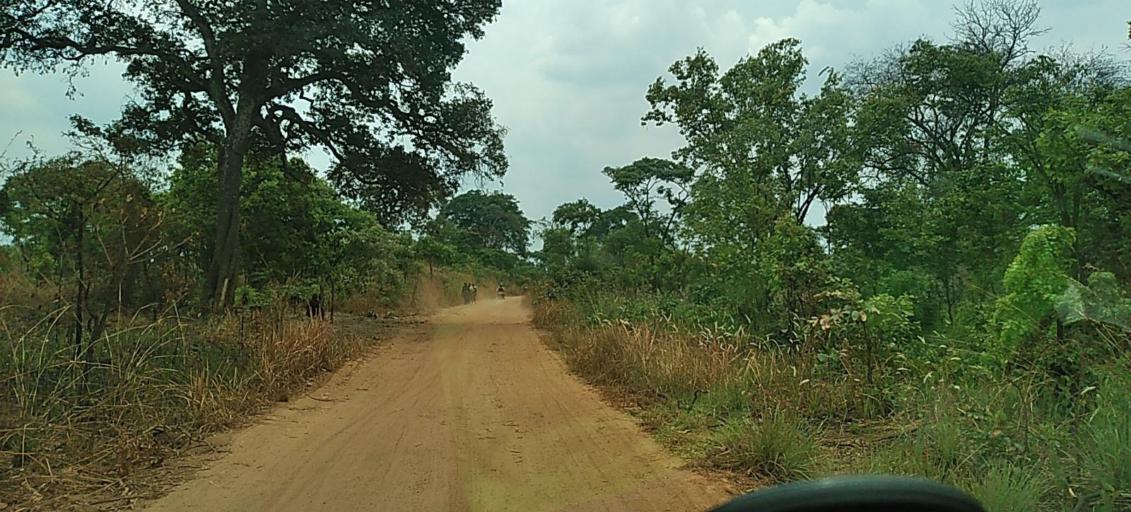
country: ZM
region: North-Western
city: Kansanshi
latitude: -12.0726
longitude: 26.3550
